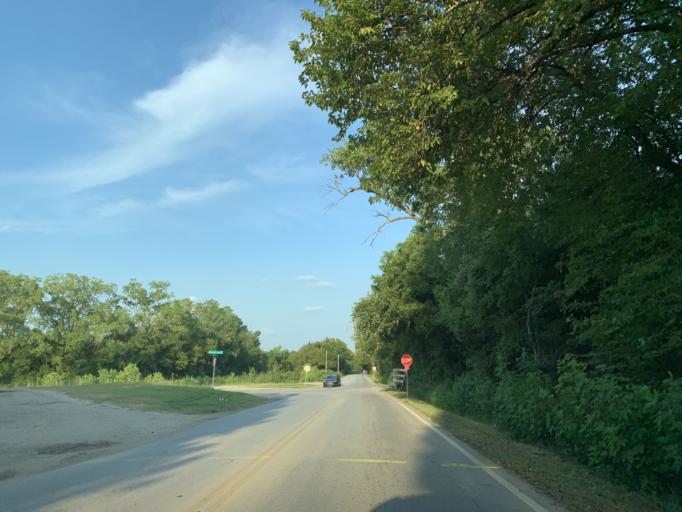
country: US
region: Texas
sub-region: Tarrant County
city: Hurst
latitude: 32.7797
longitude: -97.1797
